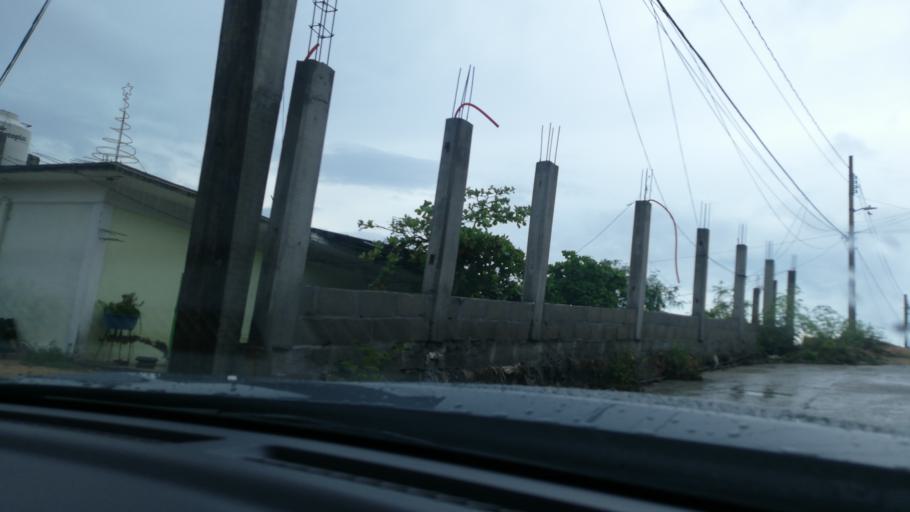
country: MX
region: Oaxaca
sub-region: Salina Cruz
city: Salina Cruz
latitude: 16.1884
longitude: -95.1948
